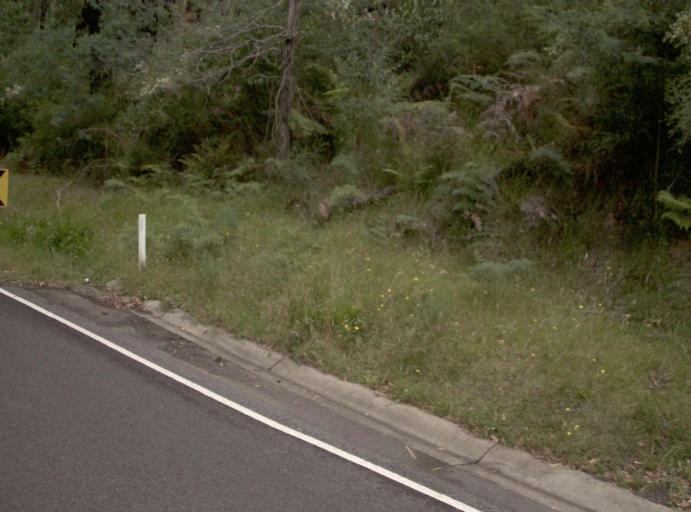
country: AU
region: Victoria
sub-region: Yarra Ranges
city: Healesville
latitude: -37.6327
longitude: 145.5883
